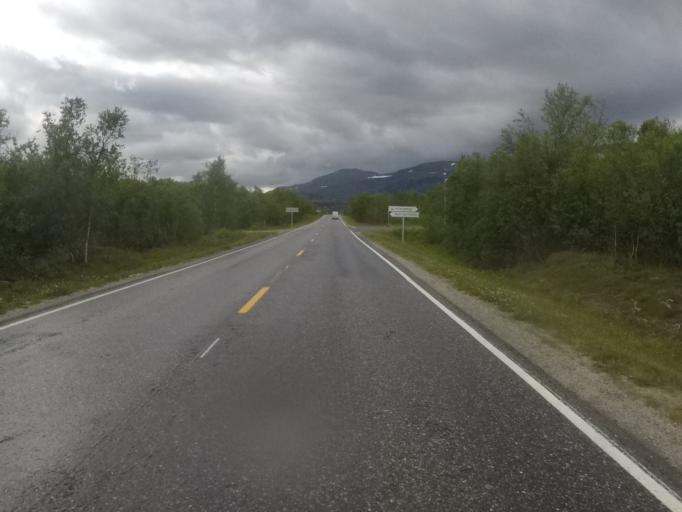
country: NO
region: Finnmark Fylke
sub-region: Porsanger
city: Lakselv
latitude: 69.9615
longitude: 24.9632
